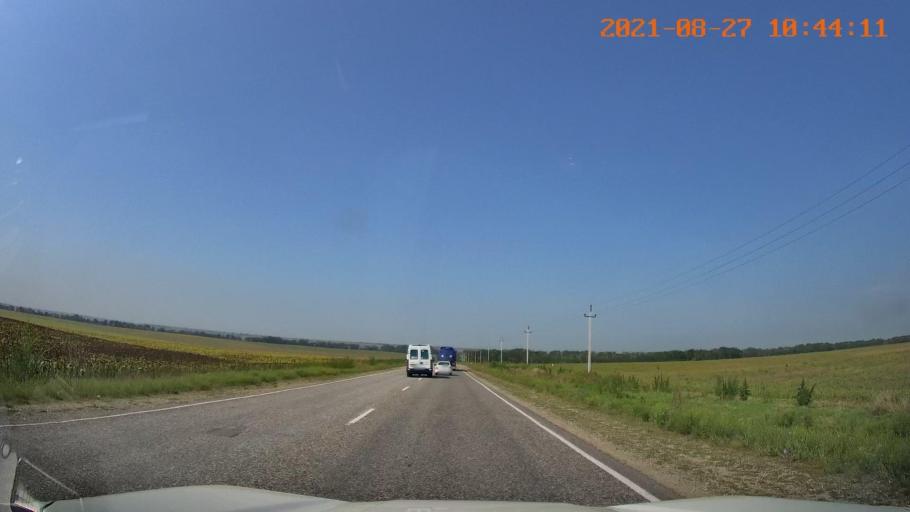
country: RU
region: Karachayevo-Cherkesiya
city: Psyzh
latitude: 44.3008
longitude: 42.0195
